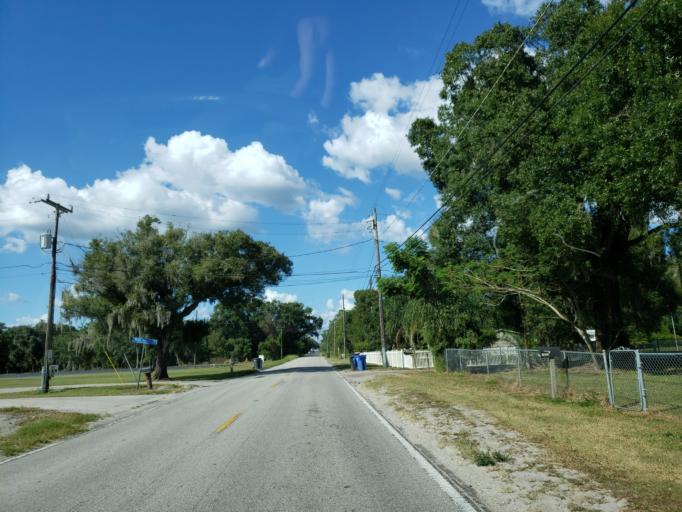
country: US
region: Florida
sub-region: Hillsborough County
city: Dover
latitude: 27.9795
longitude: -82.1869
